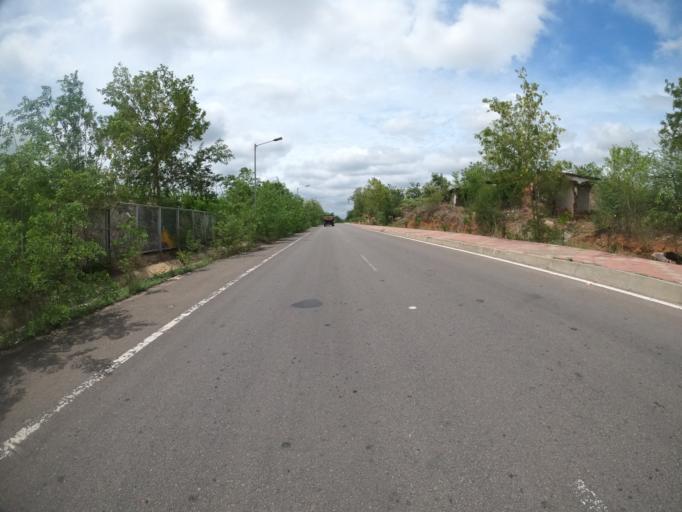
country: IN
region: Telangana
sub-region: Rangareddi
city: Balapur
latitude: 17.2777
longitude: 78.3820
